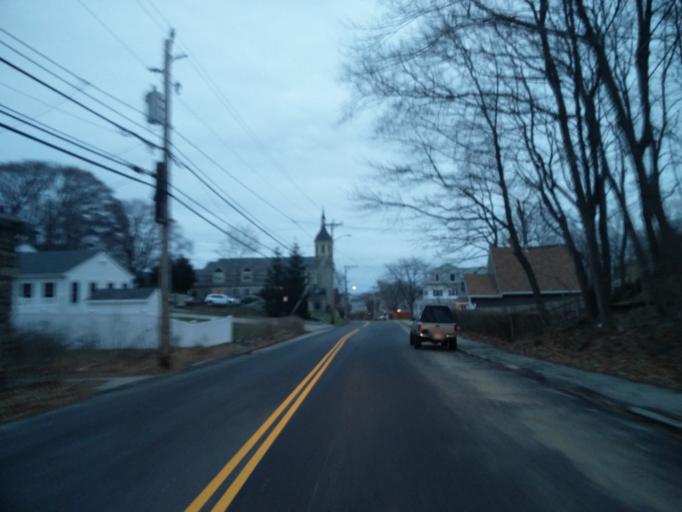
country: US
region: Massachusetts
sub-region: Norfolk County
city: Cohasset
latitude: 42.2657
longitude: -70.8450
